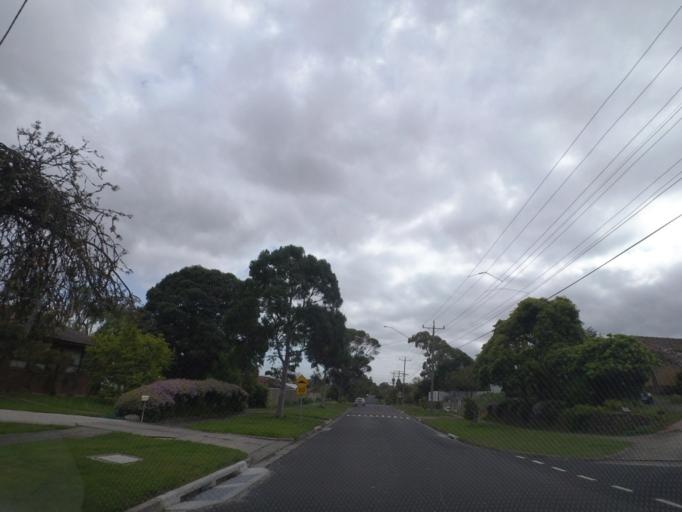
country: AU
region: Victoria
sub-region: Whitehorse
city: Nunawading
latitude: -37.8132
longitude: 145.1852
